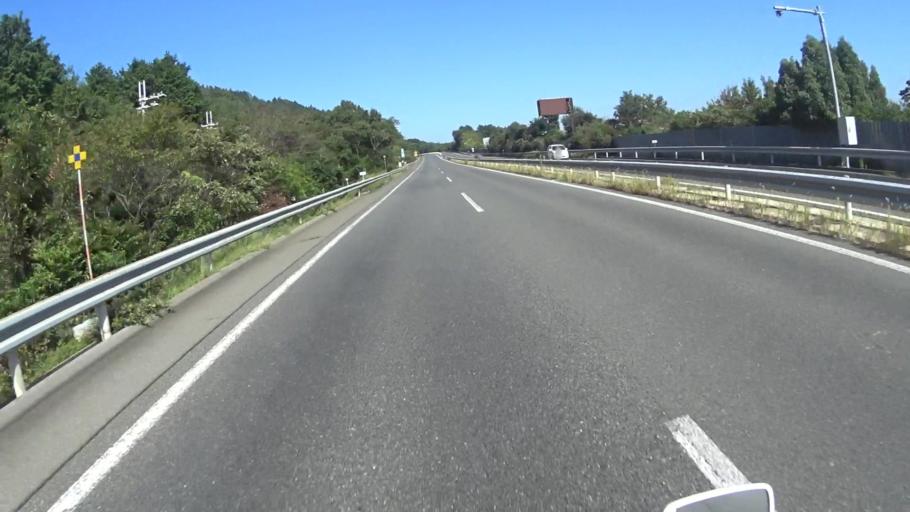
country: JP
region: Kyoto
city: Kameoka
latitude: 35.0360
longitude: 135.5422
